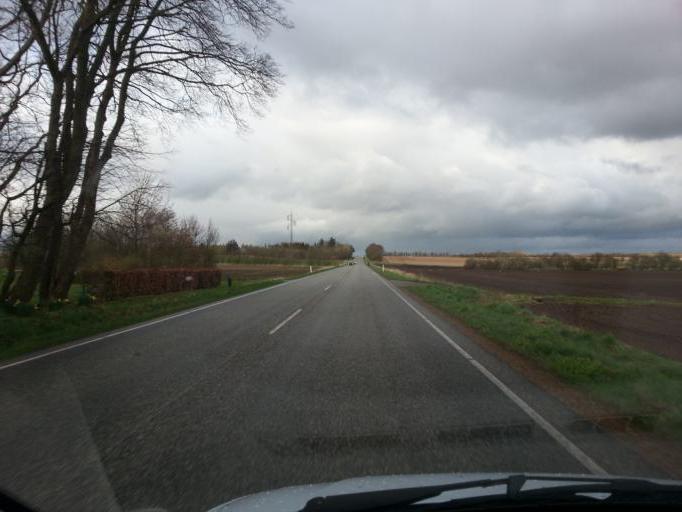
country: DK
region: Central Jutland
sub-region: Holstebro Kommune
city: Ulfborg
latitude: 56.2924
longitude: 8.3442
